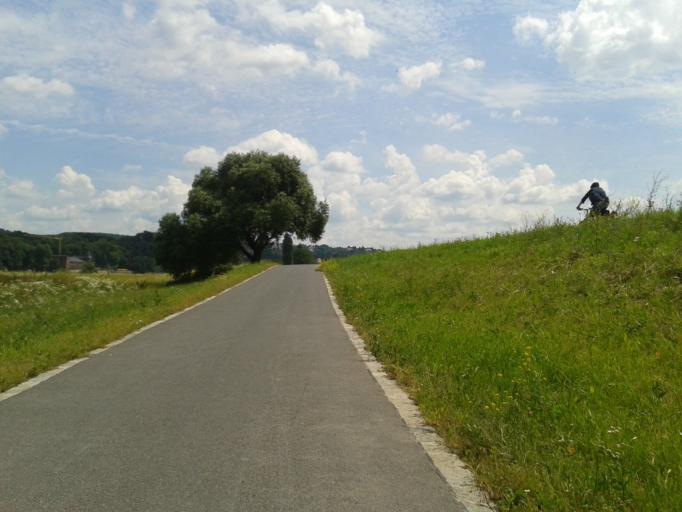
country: DE
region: Saxony
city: Albertstadt
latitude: 51.0629
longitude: 13.7772
